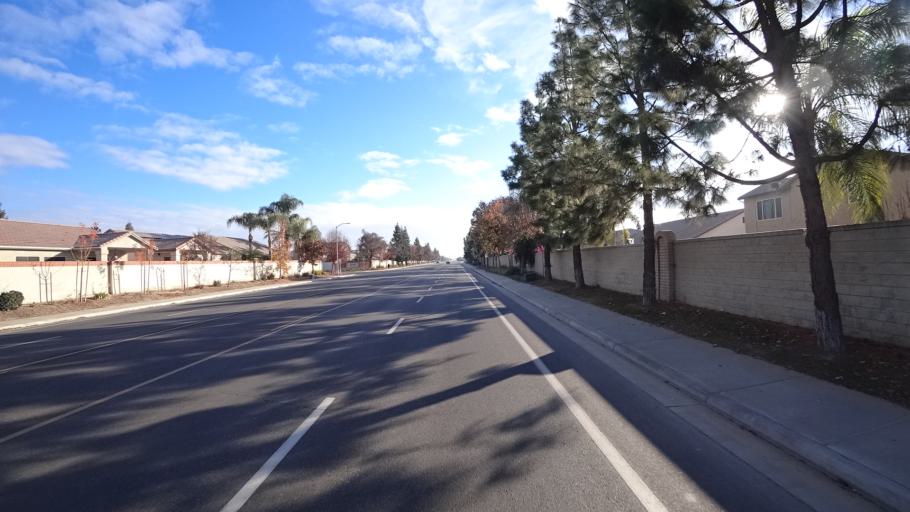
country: US
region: California
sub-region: Kern County
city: Greenacres
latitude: 35.3034
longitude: -119.1243
